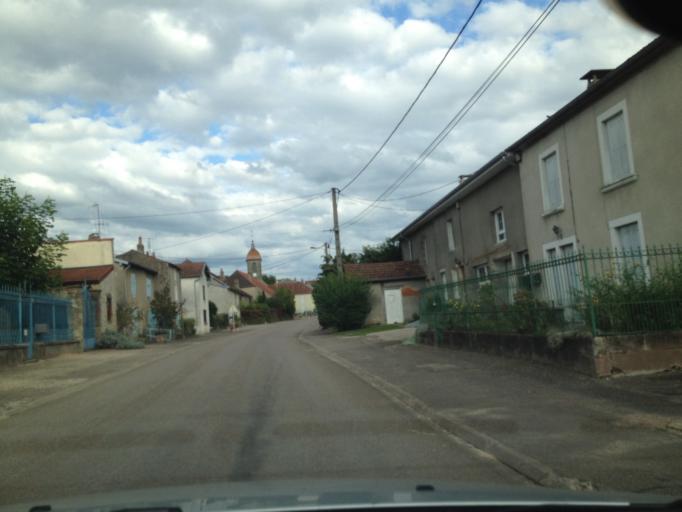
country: FR
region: Franche-Comte
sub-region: Departement de la Haute-Saone
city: Jussey
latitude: 47.8898
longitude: 5.9767
